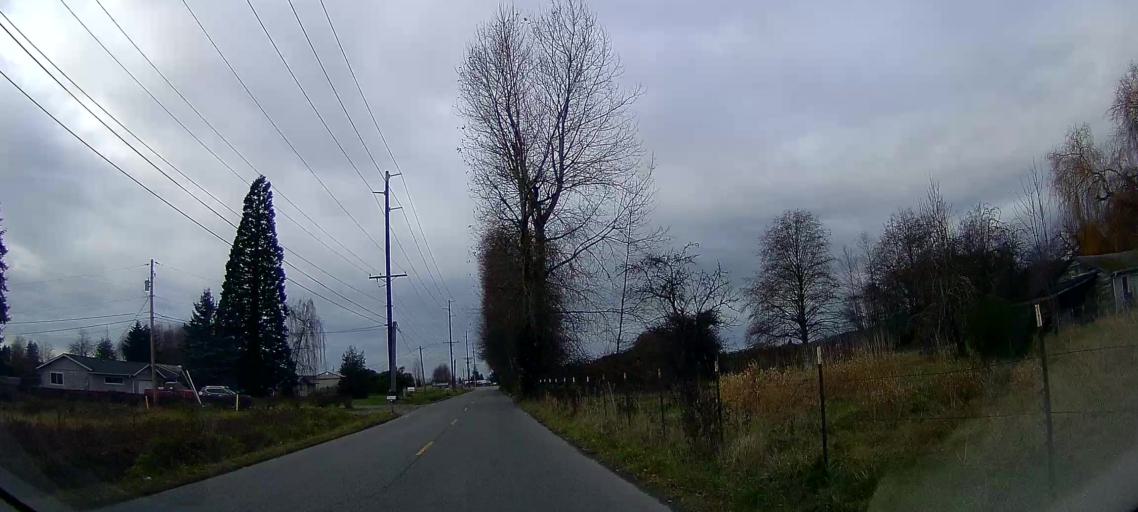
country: US
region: Washington
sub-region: Skagit County
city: Sedro-Woolley
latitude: 48.5147
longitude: -122.2509
